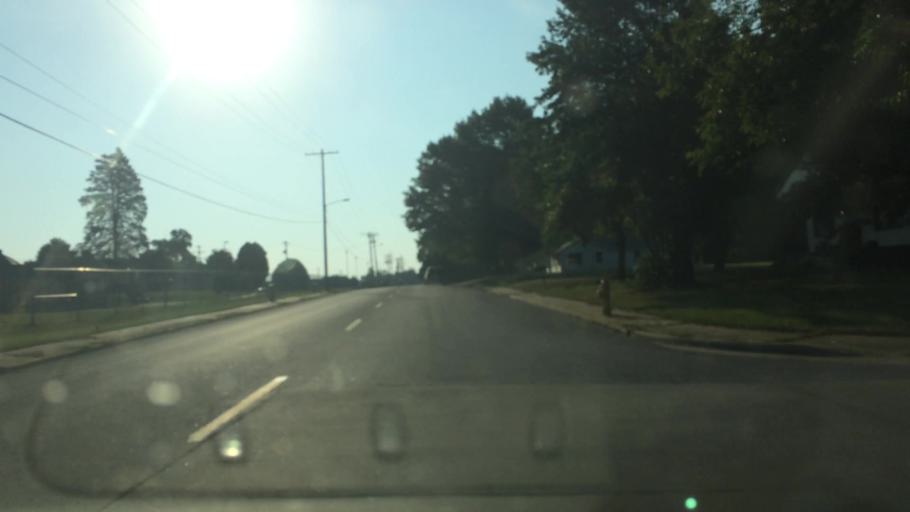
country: US
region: Missouri
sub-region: Greene County
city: Springfield
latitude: 37.2183
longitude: -93.2663
